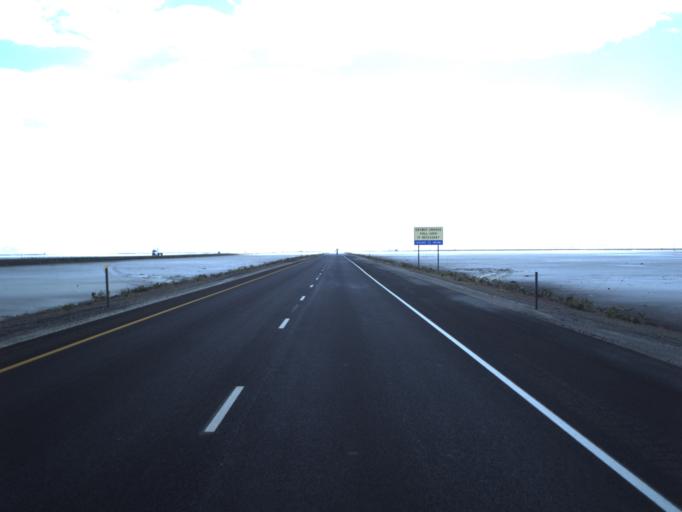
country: US
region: Utah
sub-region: Tooele County
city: Wendover
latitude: 40.7317
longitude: -113.5353
